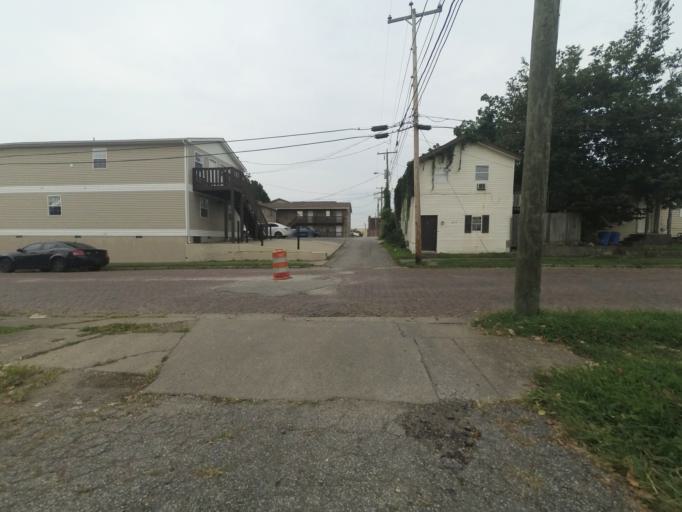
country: US
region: West Virginia
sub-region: Cabell County
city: Huntington
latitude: 38.4203
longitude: -82.4237
